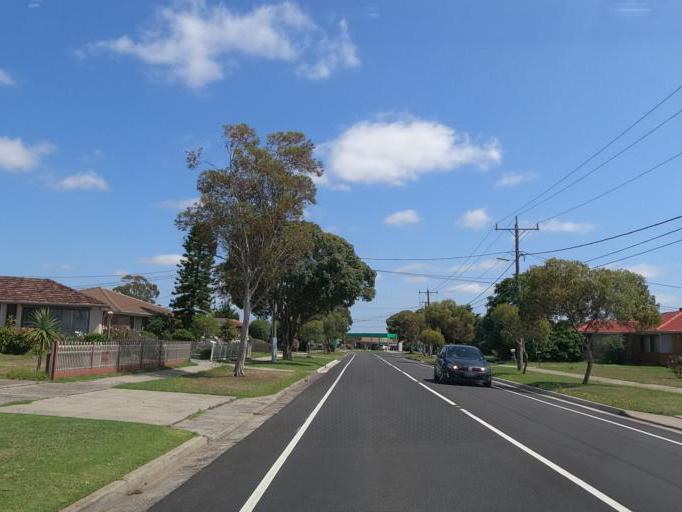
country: AU
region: Victoria
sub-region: Hume
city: Gladstone Park
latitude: -37.6903
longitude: 144.8870
